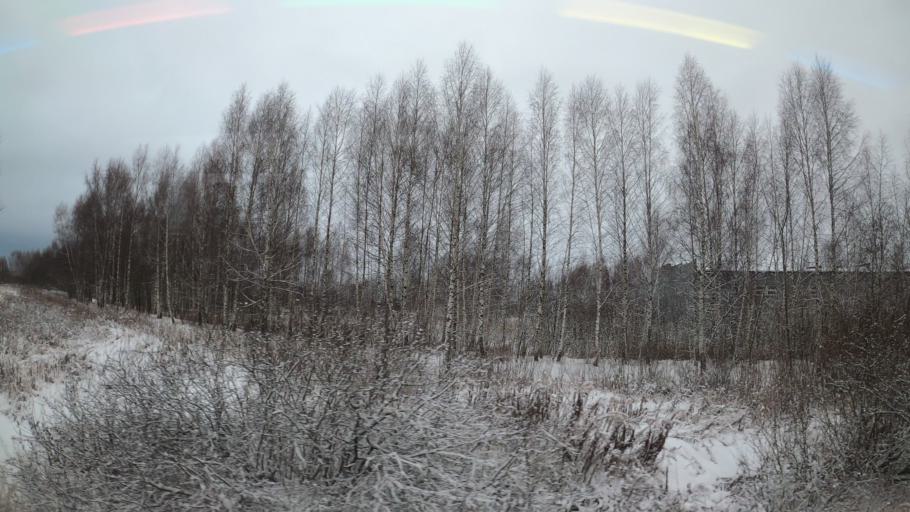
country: RU
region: Jaroslavl
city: Pereslavl'-Zalesskiy
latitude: 56.7245
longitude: 38.9049
